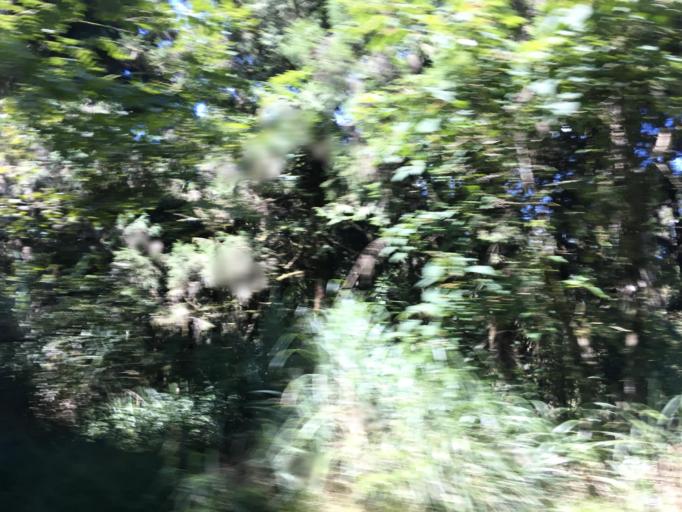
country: TW
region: Taiwan
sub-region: Yilan
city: Yilan
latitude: 24.5213
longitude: 121.5188
